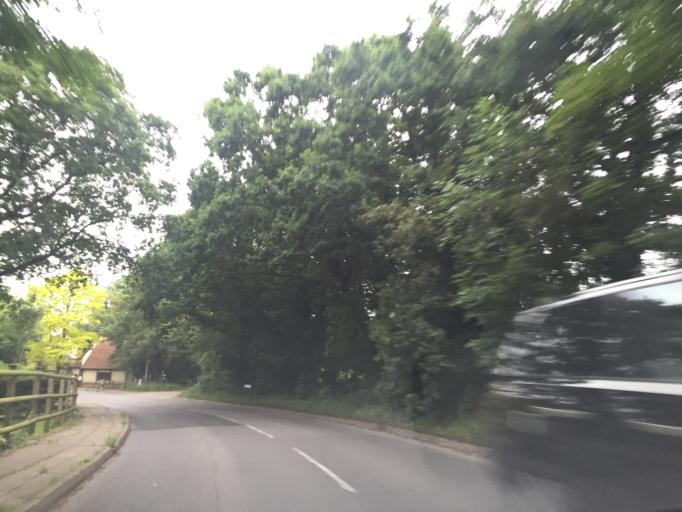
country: GB
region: England
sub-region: Greater London
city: Collier Row
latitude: 51.6260
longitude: 0.1891
